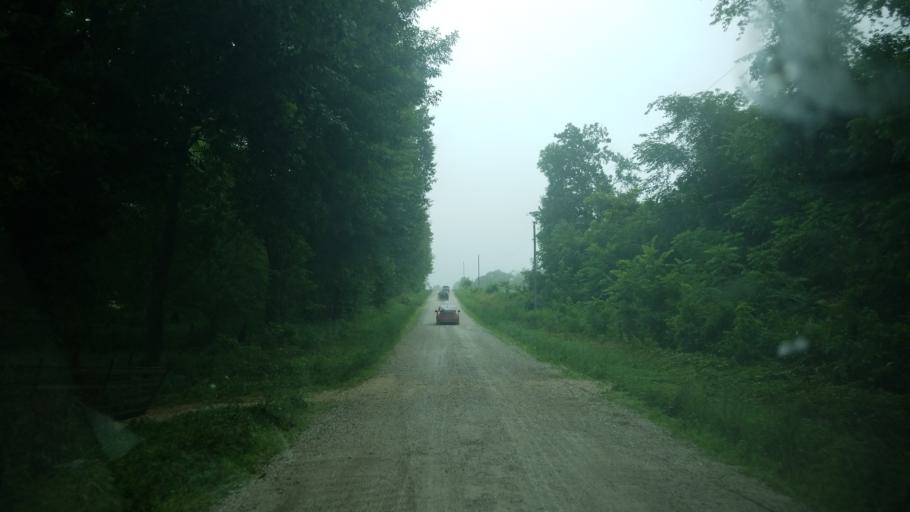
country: US
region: Missouri
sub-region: Pike County
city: Bowling Green
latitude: 39.3088
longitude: -91.3293
